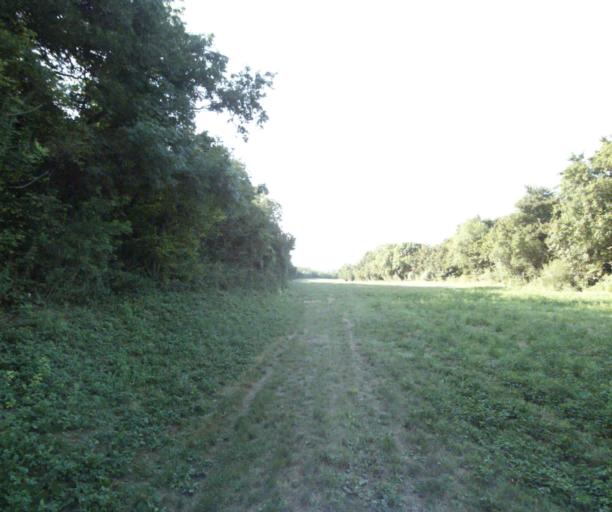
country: FR
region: Midi-Pyrenees
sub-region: Departement de la Haute-Garonne
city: Saint-Felix-Lauragais
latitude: 43.4337
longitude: 1.8242
